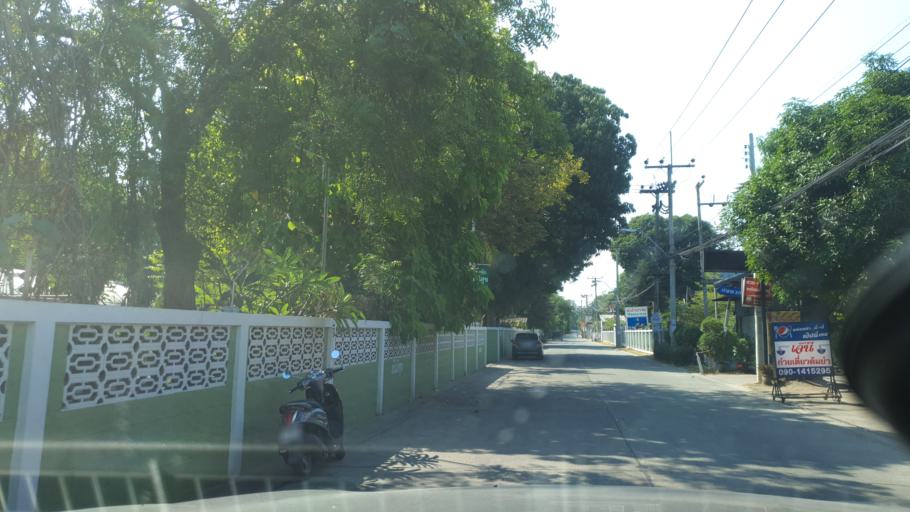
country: TH
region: Phetchaburi
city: Cha-am
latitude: 12.7896
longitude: 99.9801
